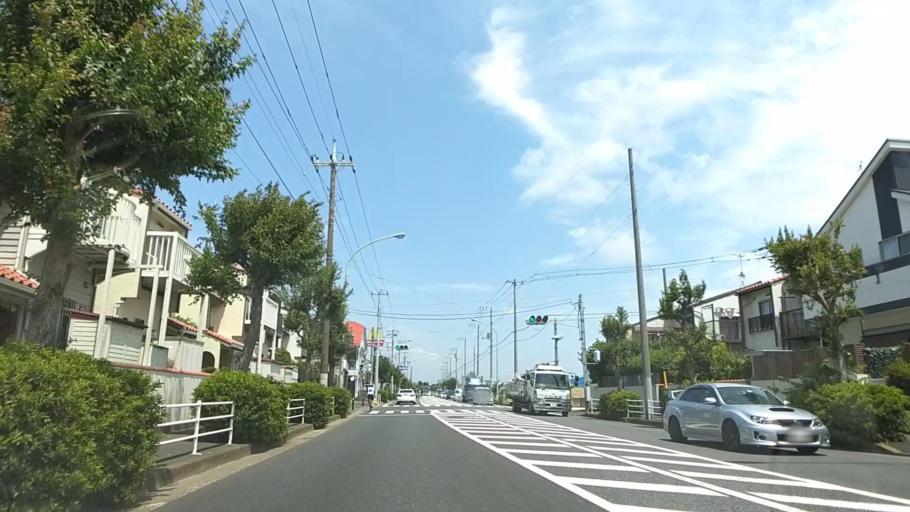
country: JP
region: Kanagawa
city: Minami-rinkan
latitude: 35.4458
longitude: 139.4842
